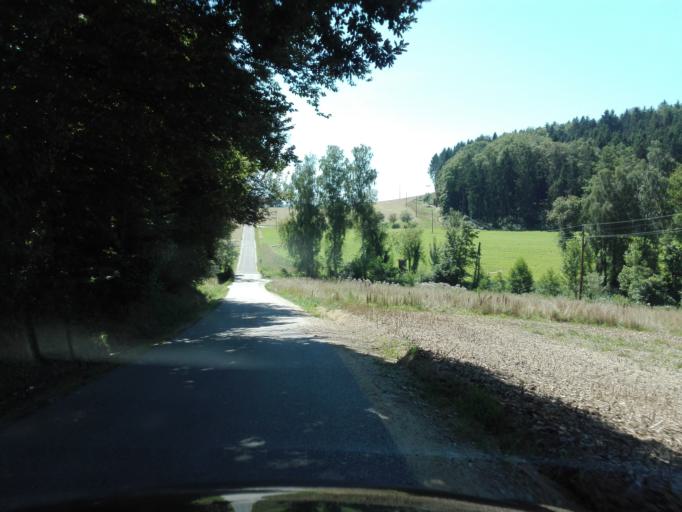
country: AT
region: Upper Austria
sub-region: Politischer Bezirk Urfahr-Umgebung
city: Gallneukirchen
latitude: 48.3196
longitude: 14.3994
